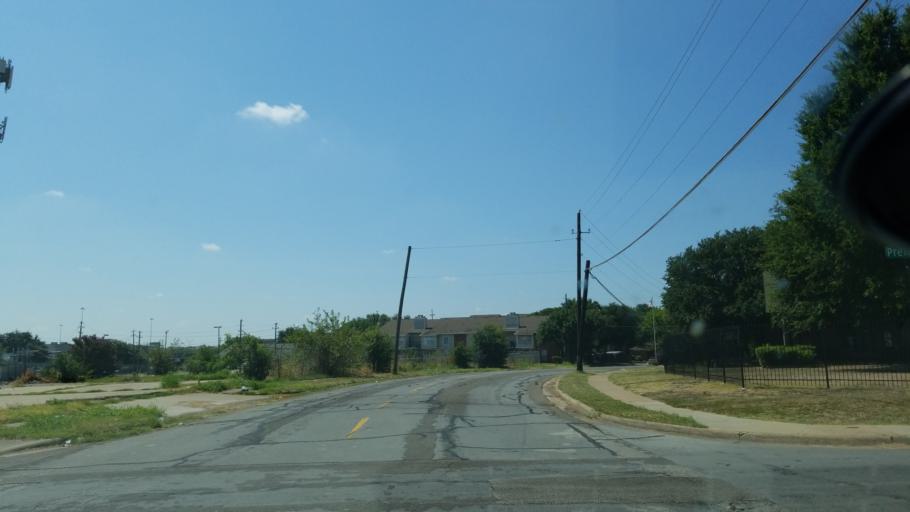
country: US
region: Texas
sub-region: Dallas County
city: Duncanville
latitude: 32.6607
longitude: -96.8841
